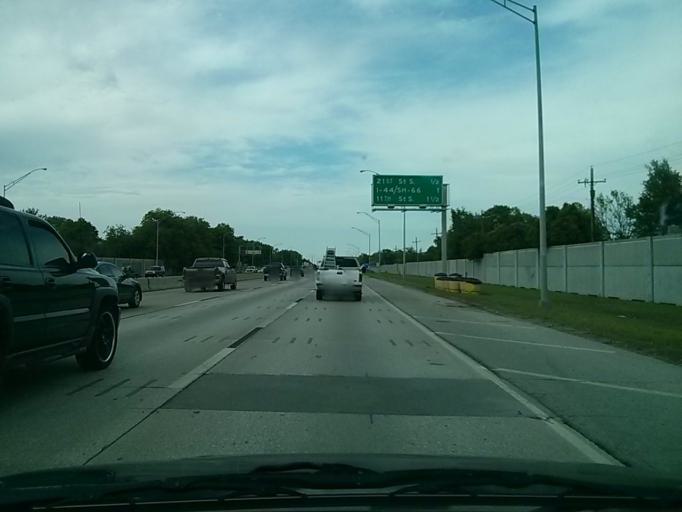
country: US
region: Oklahoma
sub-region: Tulsa County
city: Broken Arrow
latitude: 36.1217
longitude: -95.8596
